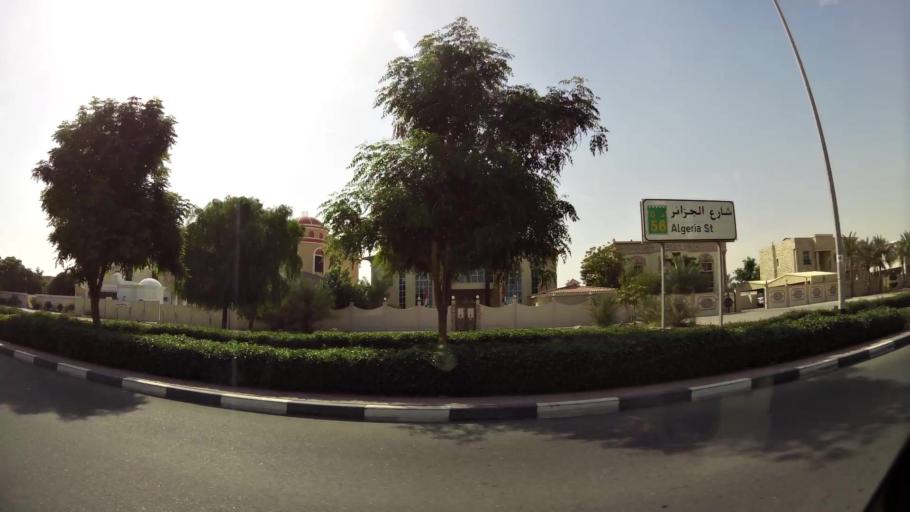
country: AE
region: Ash Shariqah
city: Sharjah
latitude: 25.2439
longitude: 55.4292
